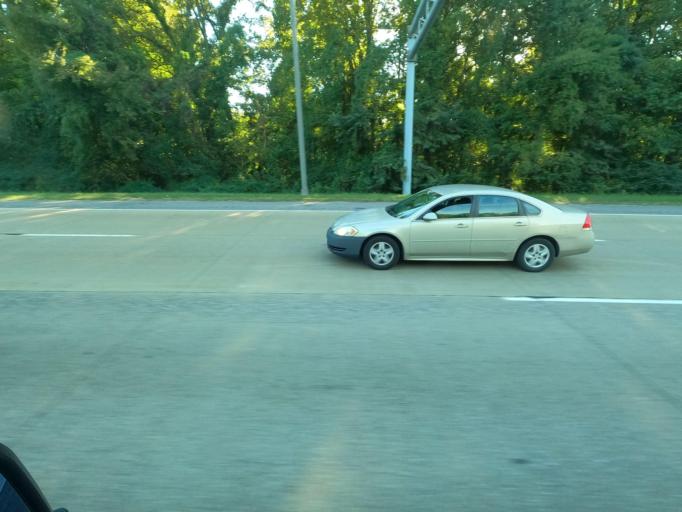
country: US
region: Tennessee
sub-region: Shelby County
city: Germantown
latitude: 35.0802
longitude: -89.8746
